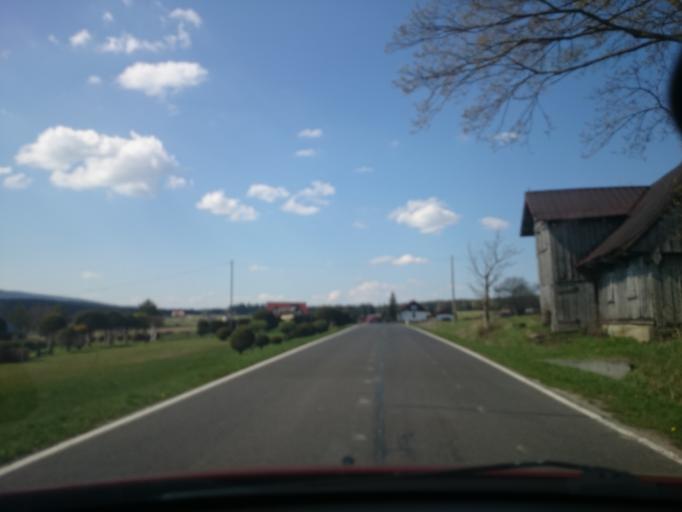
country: PL
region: Lower Silesian Voivodeship
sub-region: Powiat klodzki
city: Szczytna
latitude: 50.3089
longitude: 16.4503
